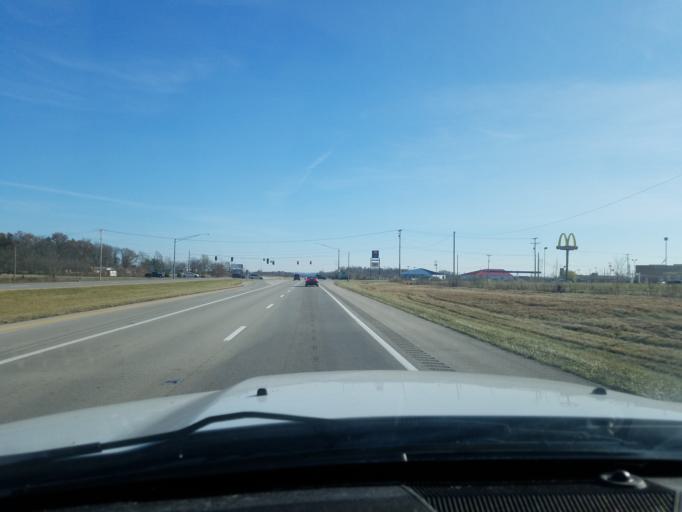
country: US
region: Ohio
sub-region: Adams County
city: Winchester
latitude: 38.9321
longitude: -83.5713
